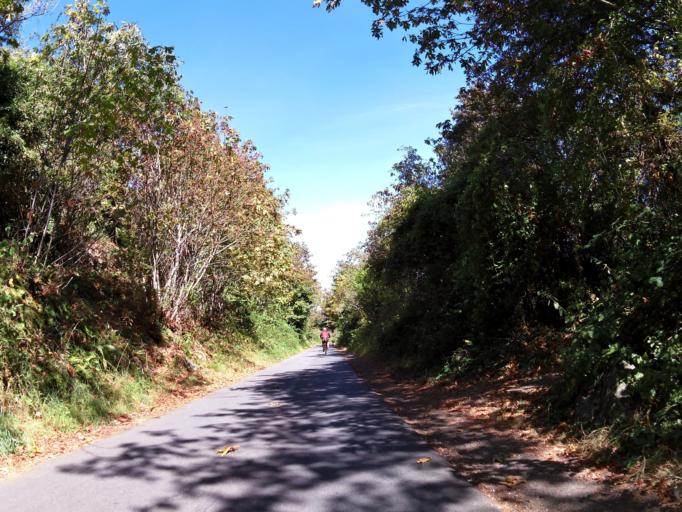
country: CA
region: British Columbia
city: Victoria
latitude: 48.4437
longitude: -123.3792
